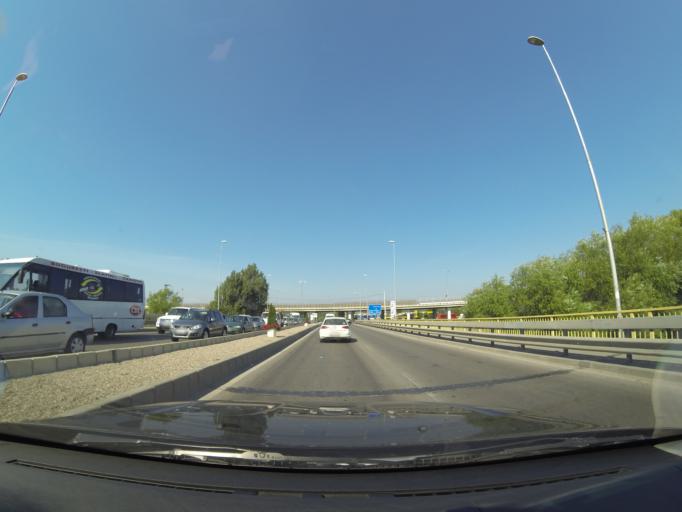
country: RO
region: Arges
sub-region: Comuna Albestii de Arges
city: Pitesti
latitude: 44.8665
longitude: 24.8810
